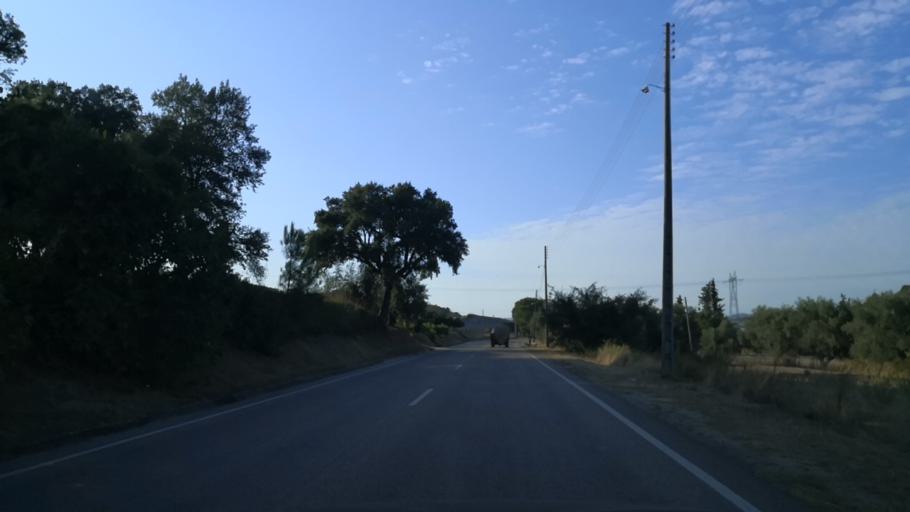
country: PT
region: Santarem
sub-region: Alcanena
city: Alcanena
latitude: 39.3686
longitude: -8.6579
